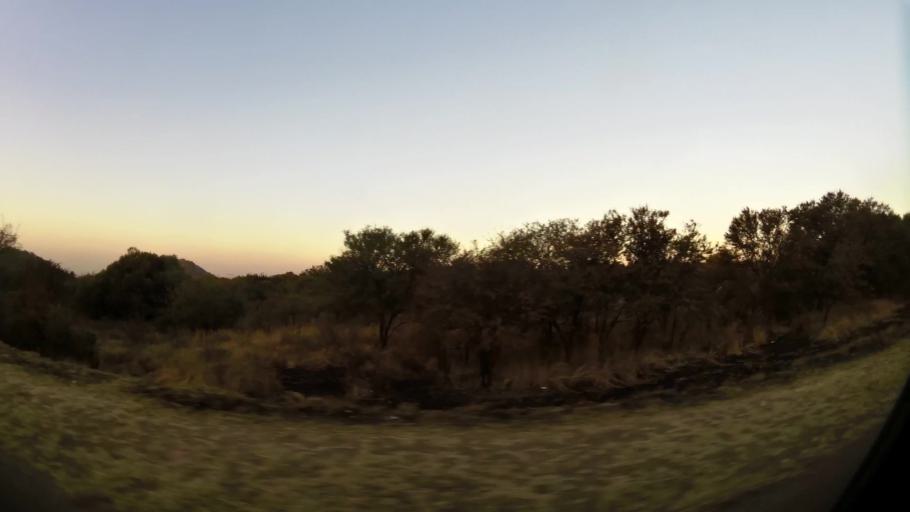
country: ZA
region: North-West
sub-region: Bojanala Platinum District Municipality
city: Rustenburg
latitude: -25.6284
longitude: 27.1867
